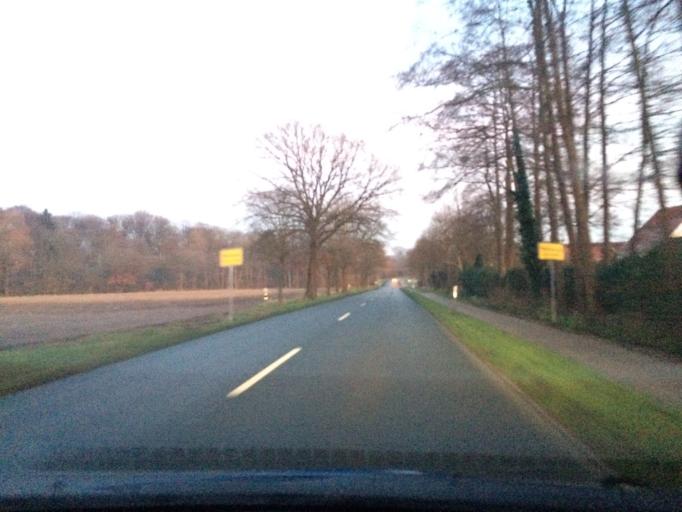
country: DE
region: Lower Saxony
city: Melbeck
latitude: 53.1814
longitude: 10.3956
